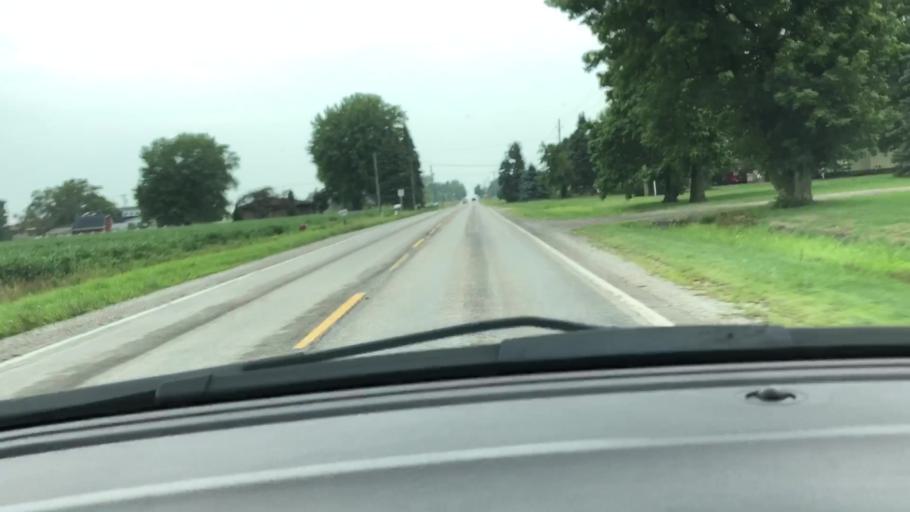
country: US
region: Michigan
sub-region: Saginaw County
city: Freeland
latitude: 43.5080
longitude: -84.0909
